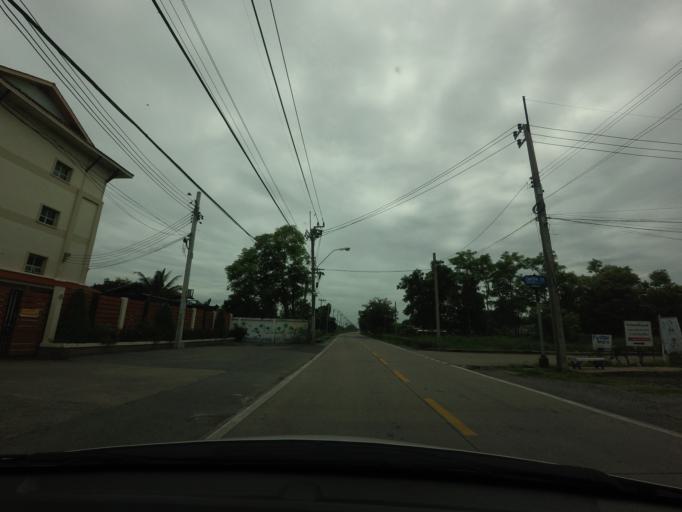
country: TH
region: Pathum Thani
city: Lam Luk Ka
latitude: 13.9189
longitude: 100.7905
